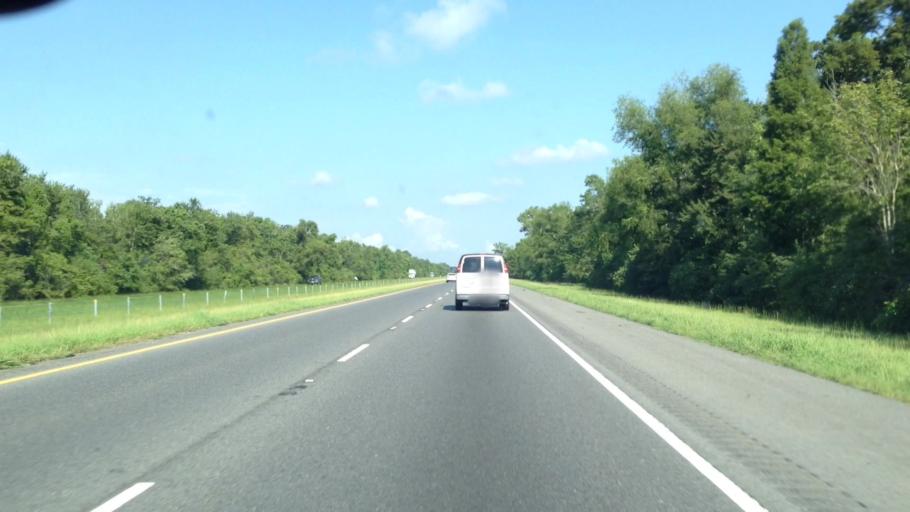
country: US
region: Louisiana
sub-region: Saint James Parish
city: Grand Point
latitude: 30.1383
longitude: -90.7414
